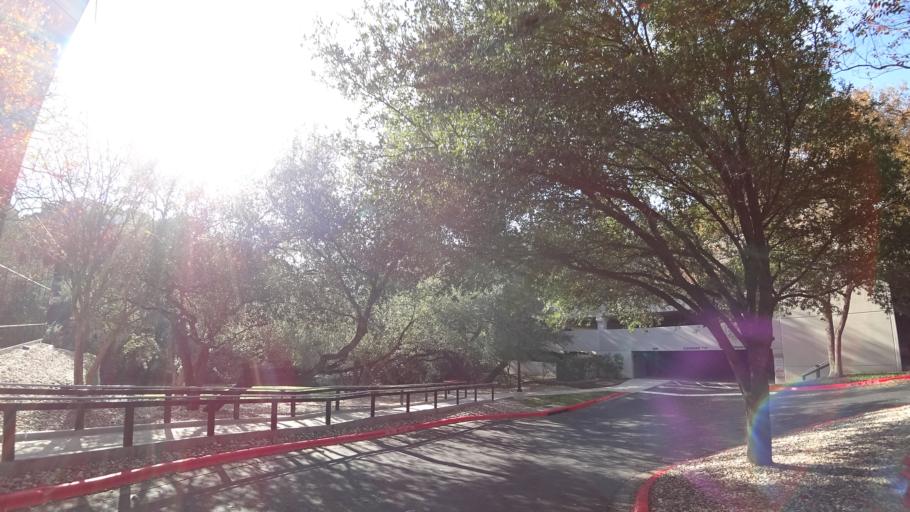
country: US
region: Texas
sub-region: Williamson County
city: Jollyville
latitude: 30.3869
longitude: -97.7605
